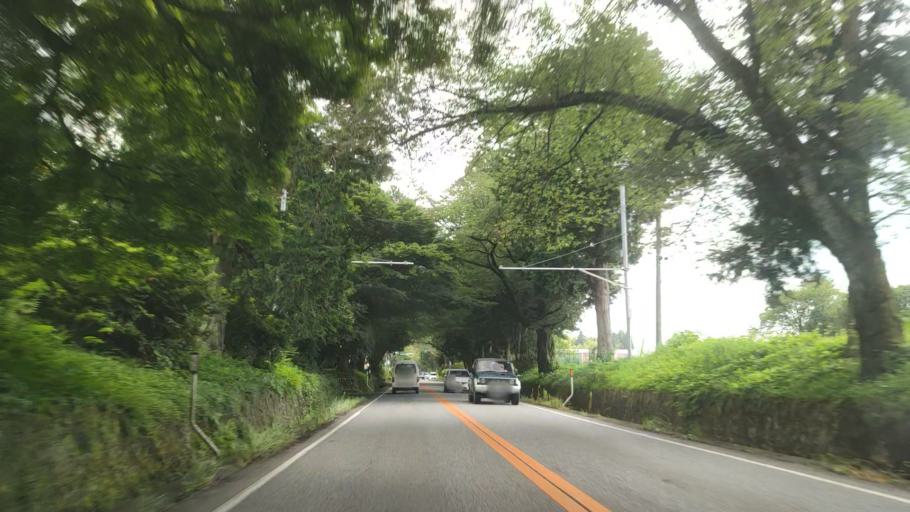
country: JP
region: Tochigi
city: Utsunomiya-shi
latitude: 36.6321
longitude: 139.8508
